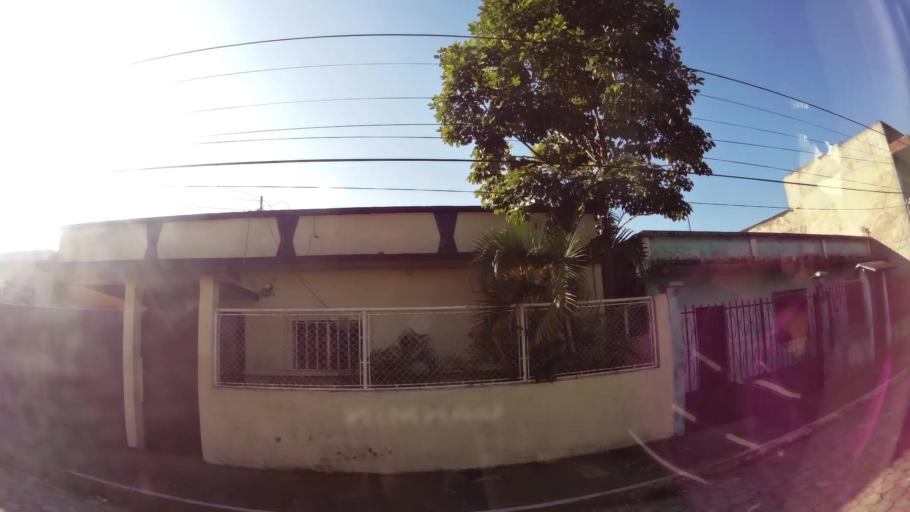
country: GT
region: Suchitepeque
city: Mazatenango
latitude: 14.5306
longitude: -91.5149
